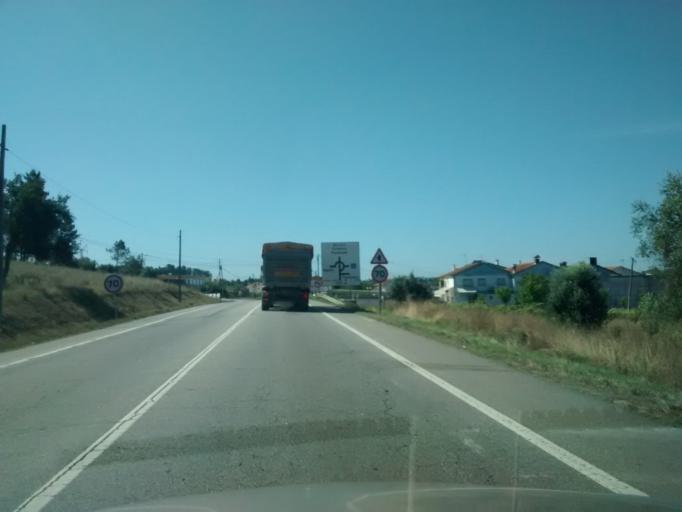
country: PT
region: Aveiro
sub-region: Anadia
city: Anadia
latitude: 40.4191
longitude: -8.4542
